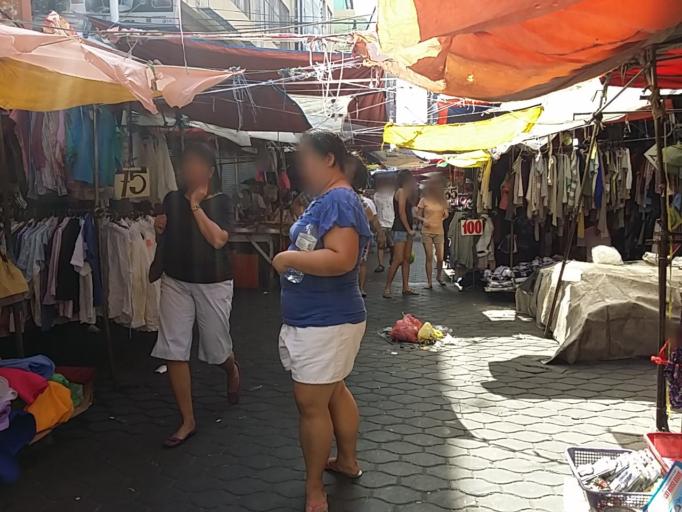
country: PH
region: Metro Manila
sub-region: City of Manila
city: Quiapo
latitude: 14.5983
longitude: 120.9825
